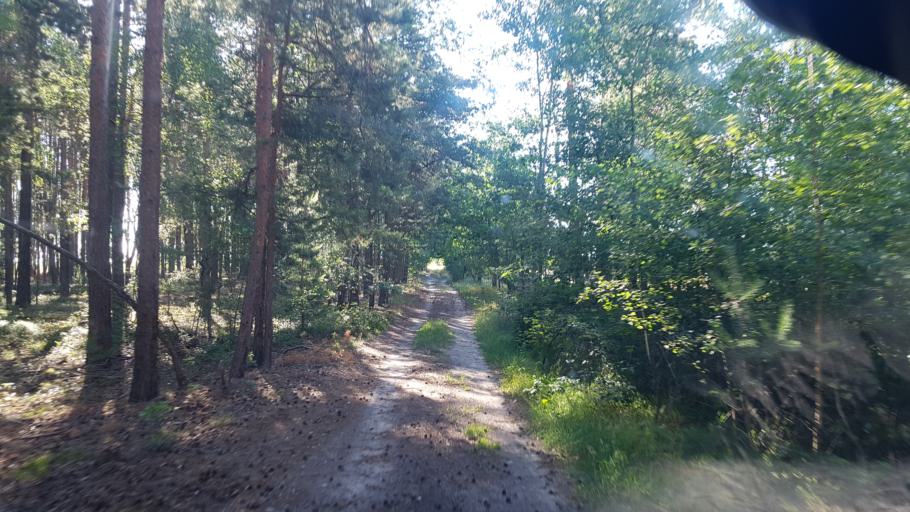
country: DE
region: Brandenburg
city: Sallgast
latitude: 51.6068
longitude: 13.7855
